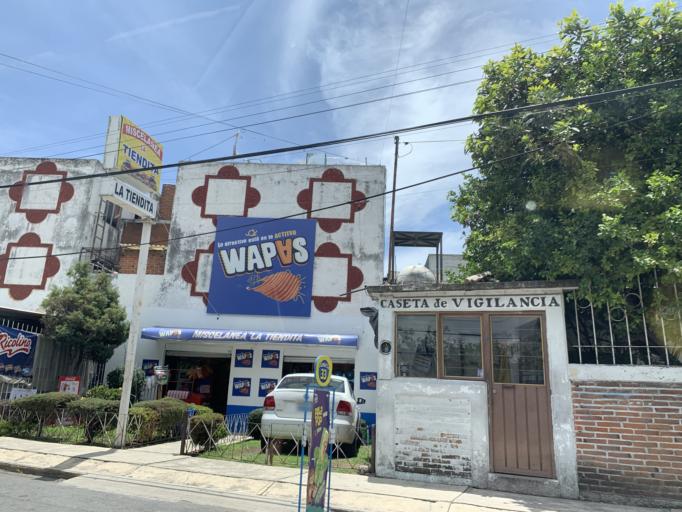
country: MX
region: Puebla
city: Puebla
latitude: 19.0701
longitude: -98.2028
